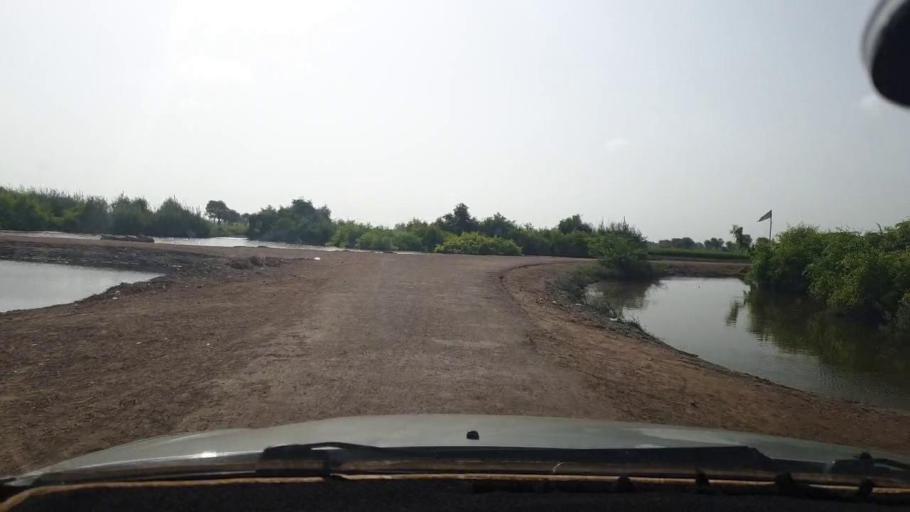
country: PK
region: Sindh
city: Tando Bago
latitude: 24.8075
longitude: 68.9161
